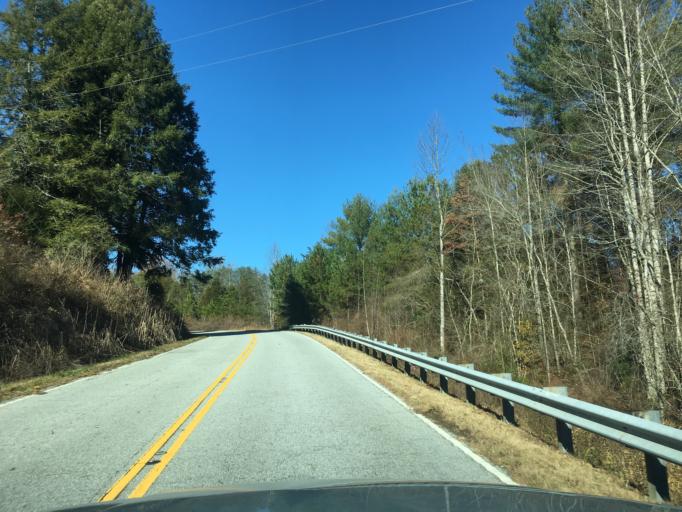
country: US
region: South Carolina
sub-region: Oconee County
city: Walhalla
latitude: 34.9315
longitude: -82.9895
